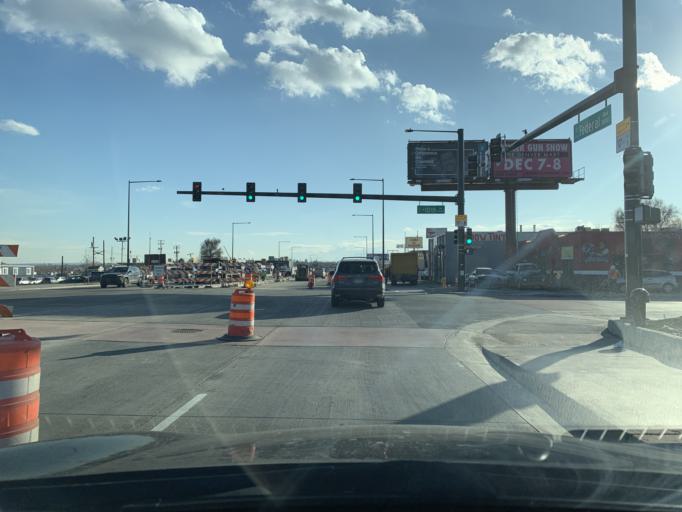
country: US
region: Colorado
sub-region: Denver County
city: Denver
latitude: 39.7332
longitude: -105.0252
